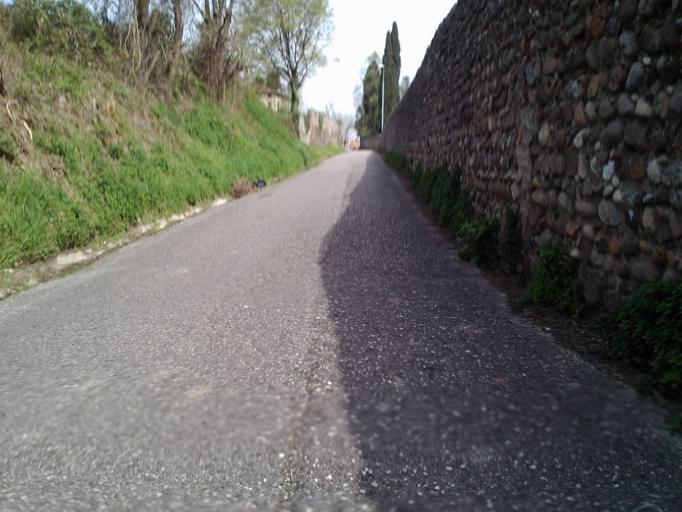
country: IT
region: Veneto
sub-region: Provincia di Verona
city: Sommacampagna
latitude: 45.4039
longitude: 10.8411
